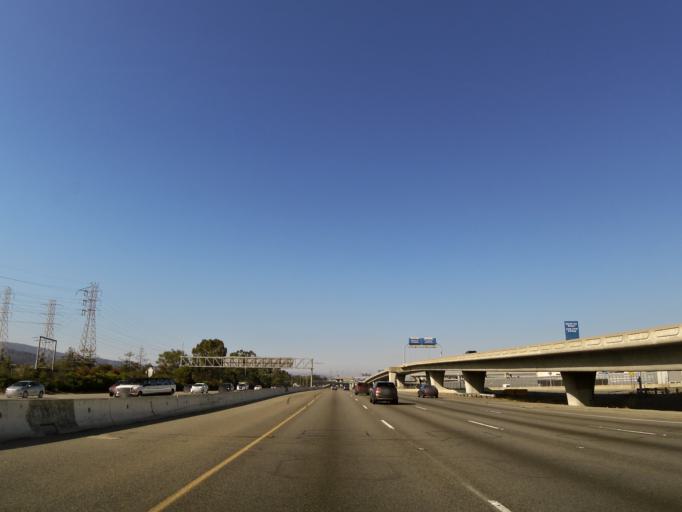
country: US
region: California
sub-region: San Mateo County
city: Millbrae
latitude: 37.6081
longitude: -122.3889
